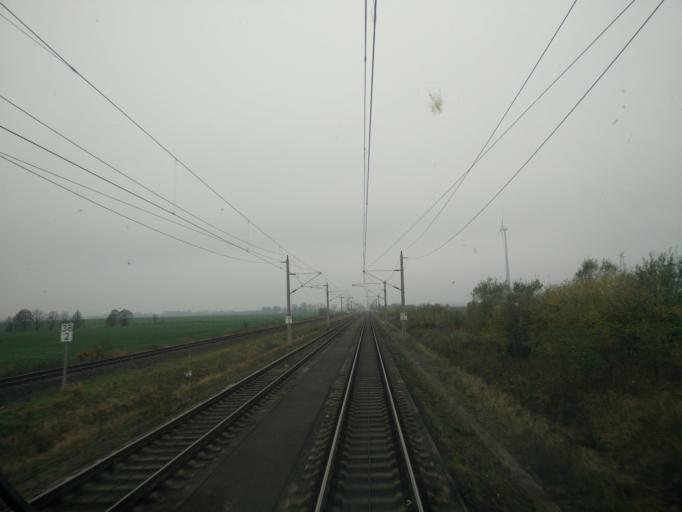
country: DE
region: Brandenburg
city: Nauen
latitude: 52.5680
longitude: 12.8298
